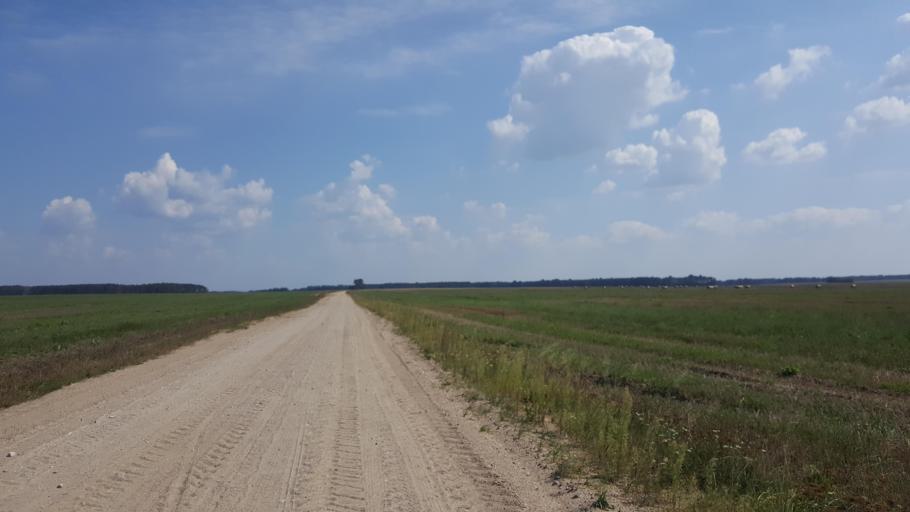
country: BY
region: Brest
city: Kamyanyuki
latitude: 52.4910
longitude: 23.5916
